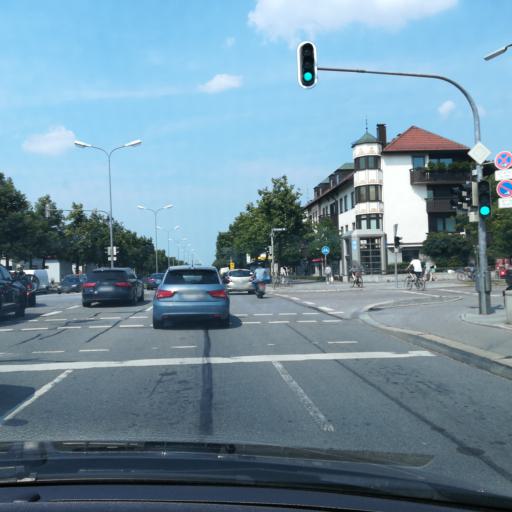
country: DE
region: Bavaria
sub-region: Upper Bavaria
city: Neuried
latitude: 48.1161
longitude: 11.5026
